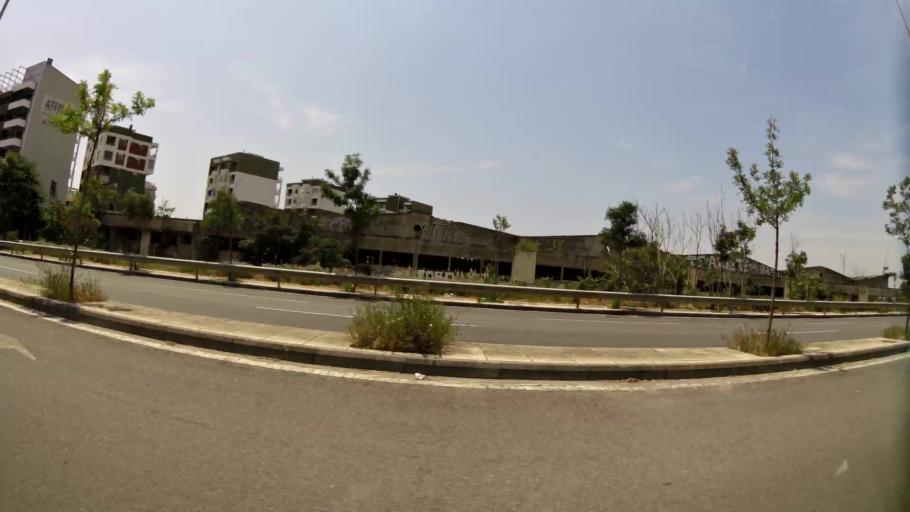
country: GR
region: Central Macedonia
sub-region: Nomos Thessalonikis
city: Ampelokipoi
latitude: 40.6470
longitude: 22.9155
